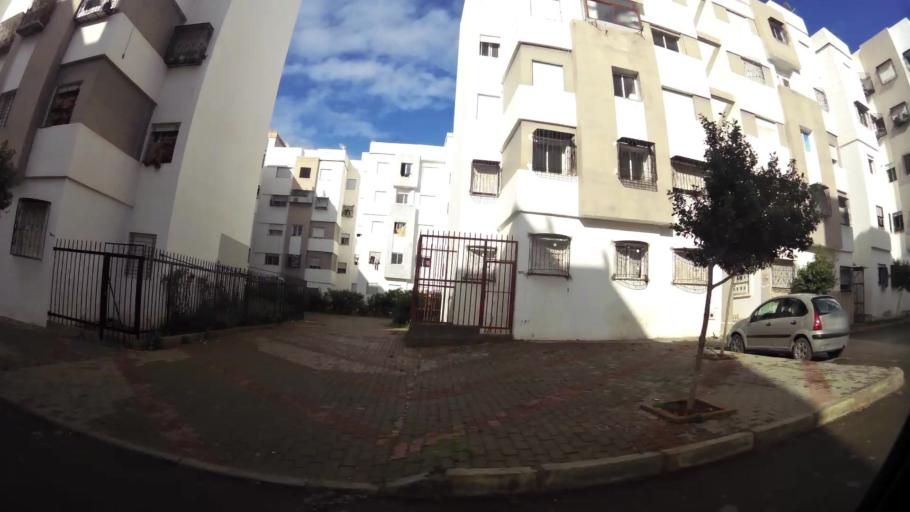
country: MA
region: Grand Casablanca
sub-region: Casablanca
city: Casablanca
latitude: 33.5564
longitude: -7.7010
